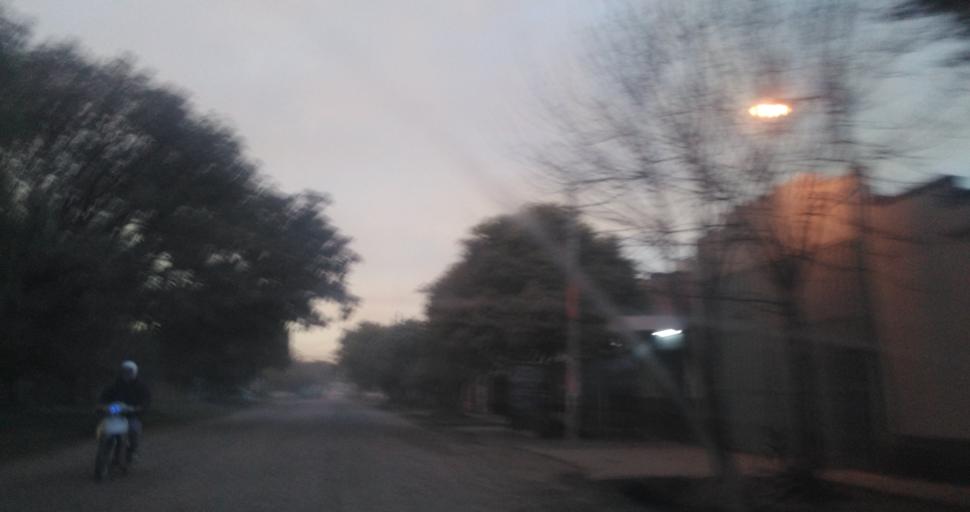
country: AR
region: Chaco
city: Fontana
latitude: -27.4368
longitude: -59.0221
